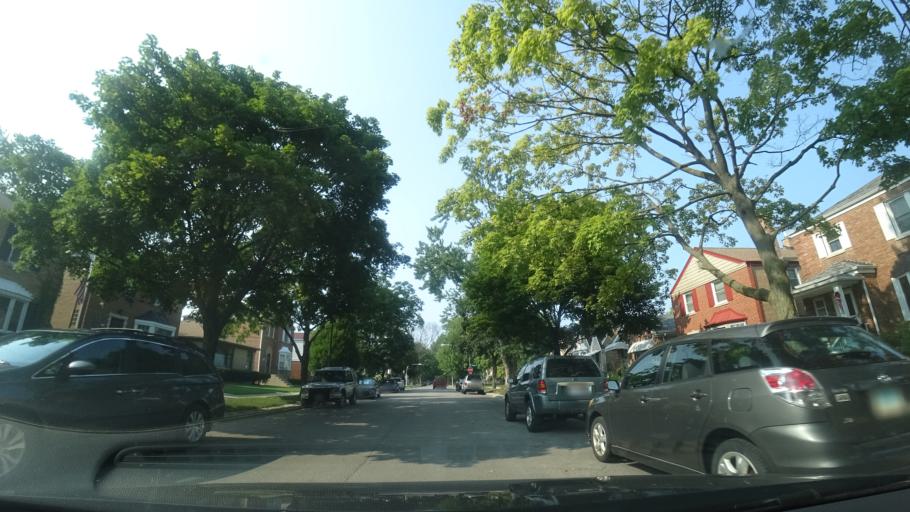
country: US
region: Illinois
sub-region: Cook County
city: Lincolnwood
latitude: 41.9930
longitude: -87.7325
